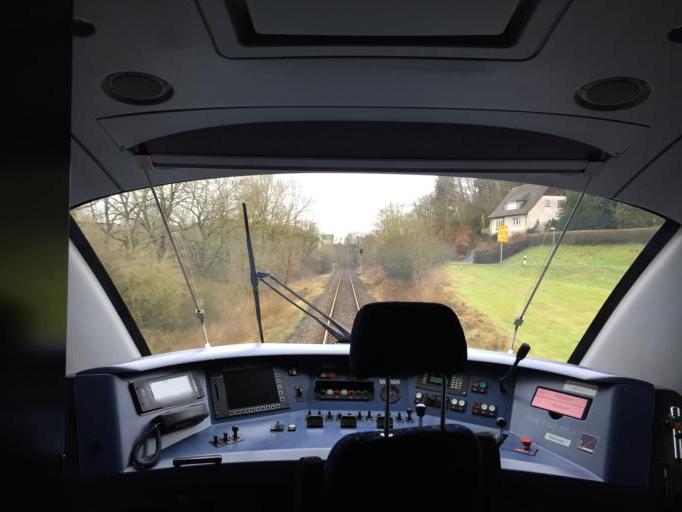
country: DE
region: Hesse
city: Frankenberg
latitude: 51.0683
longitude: 8.8030
